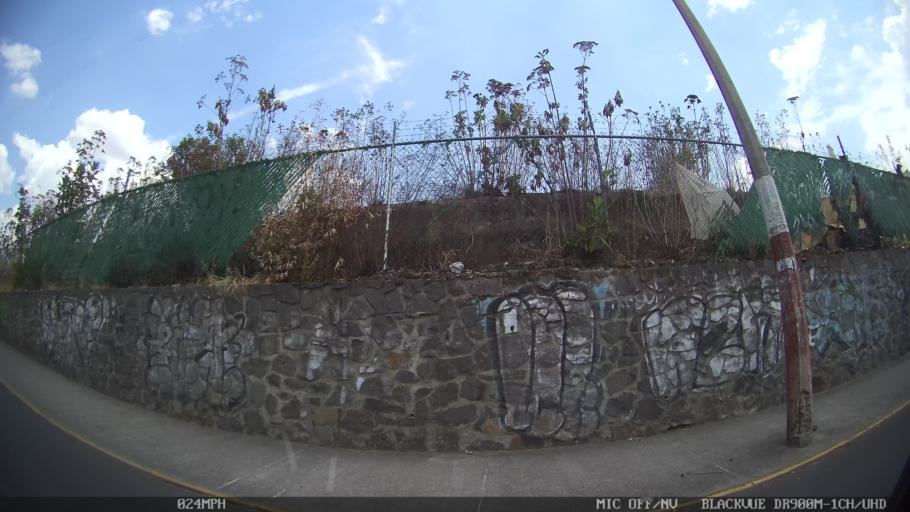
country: MX
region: Jalisco
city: Tonala
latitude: 20.6287
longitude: -103.2568
